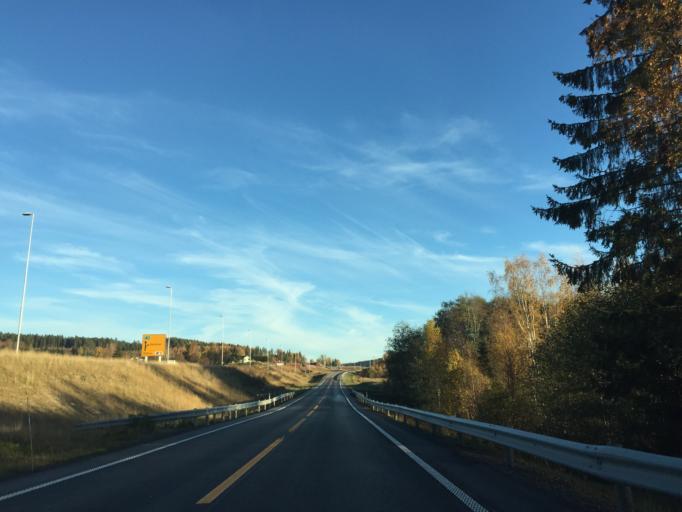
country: NO
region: Hedmark
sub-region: Kongsvinger
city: Spetalen
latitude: 60.2135
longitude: 11.8765
